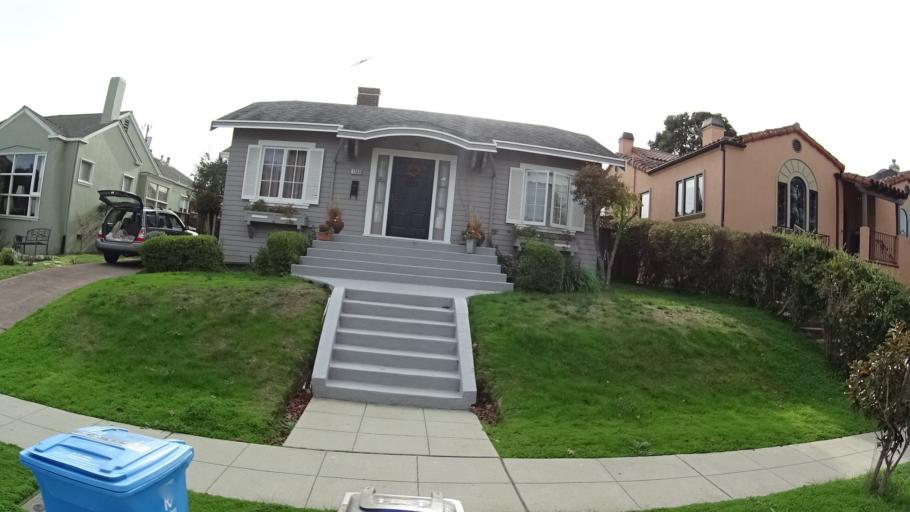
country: US
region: California
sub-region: San Mateo County
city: Burlingame
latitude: 37.5828
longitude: -122.3747
